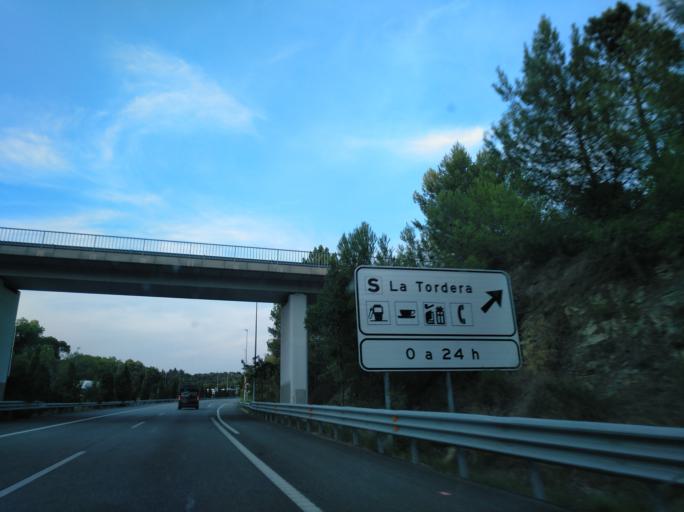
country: ES
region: Catalonia
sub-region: Provincia de Barcelona
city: Santa Susanna
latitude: 41.6654
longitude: 2.7132
